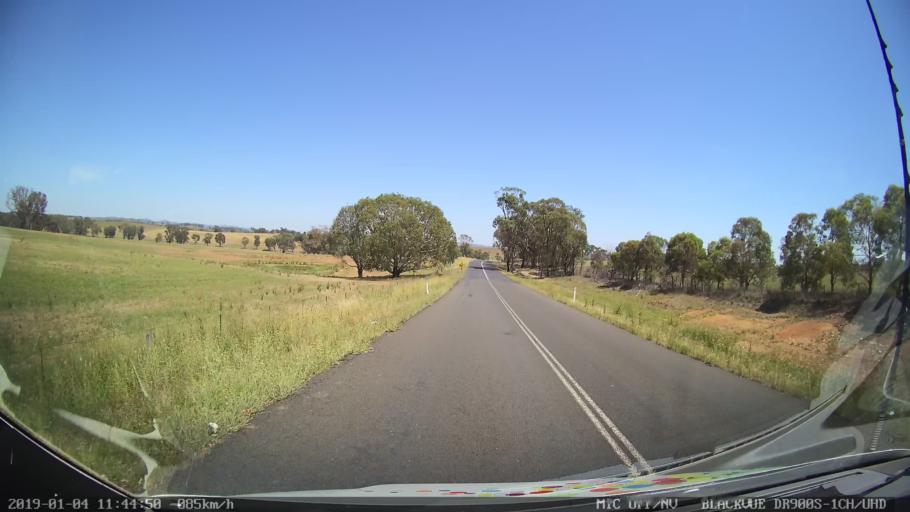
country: AU
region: New South Wales
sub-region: Cabonne
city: Molong
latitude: -32.9606
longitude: 148.7675
